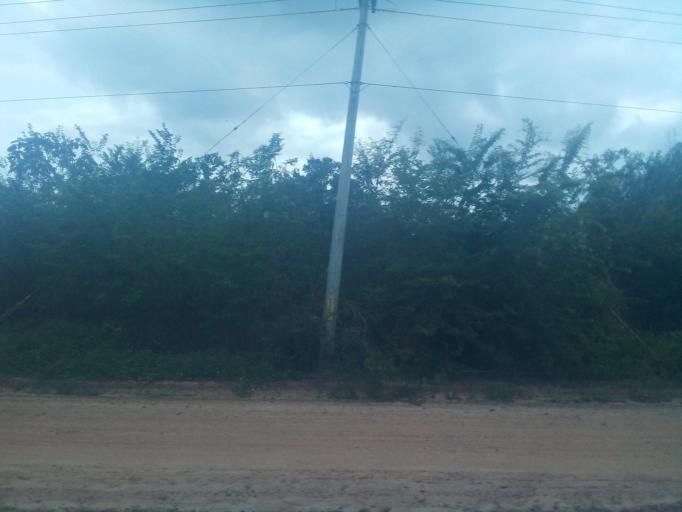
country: BR
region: Maranhao
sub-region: Itapecuru Mirim
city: Itapecuru Mirim
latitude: -3.1121
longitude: -44.3291
